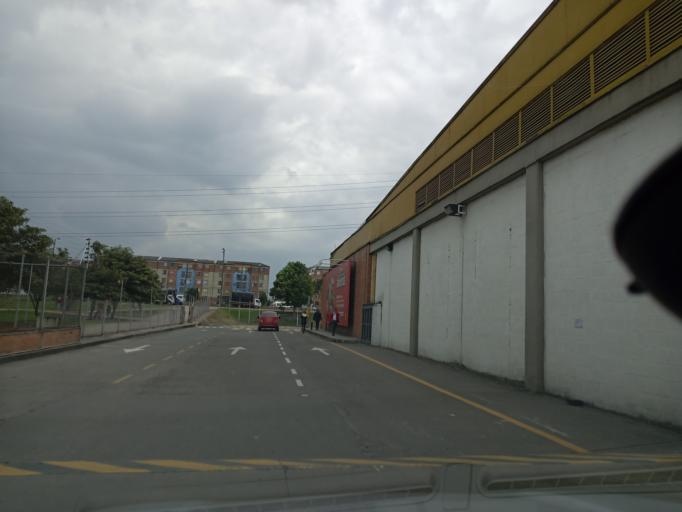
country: CO
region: Cundinamarca
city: Funza
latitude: 4.6723
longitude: -74.1536
